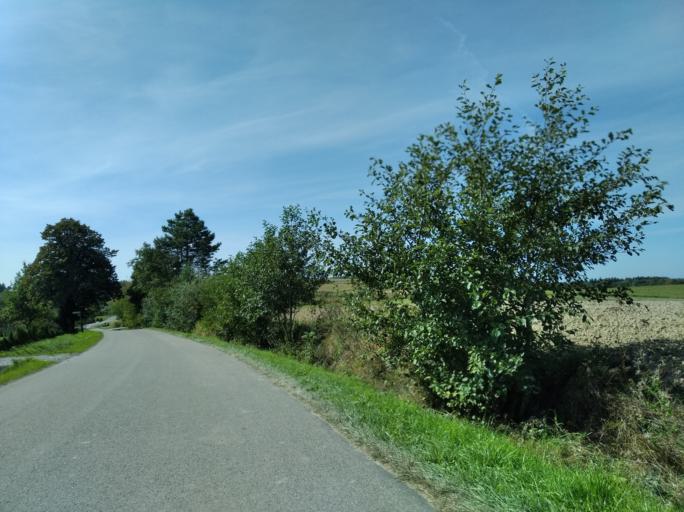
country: PL
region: Subcarpathian Voivodeship
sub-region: Powiat ropczycko-sedziszowski
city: Wielopole Skrzynskie
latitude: 49.9142
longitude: 21.6076
